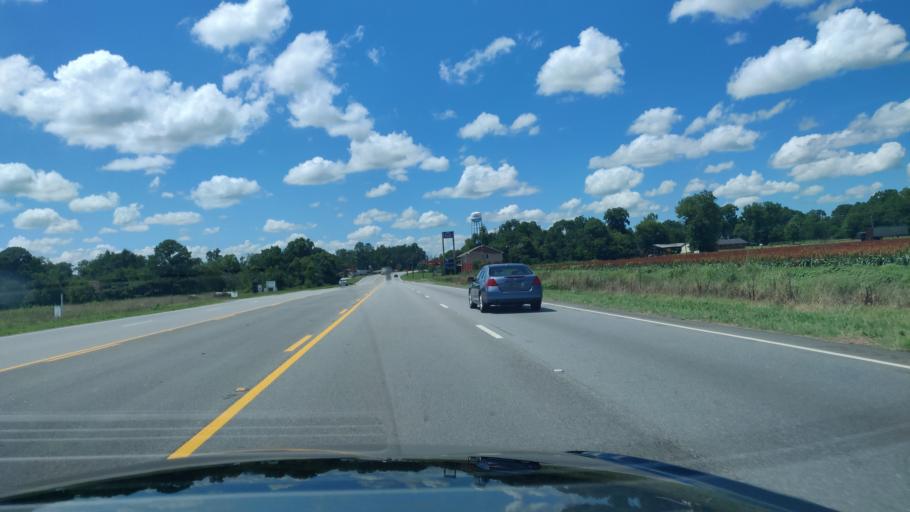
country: US
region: Georgia
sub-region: Terrell County
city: Dawson
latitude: 31.7157
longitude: -84.3453
